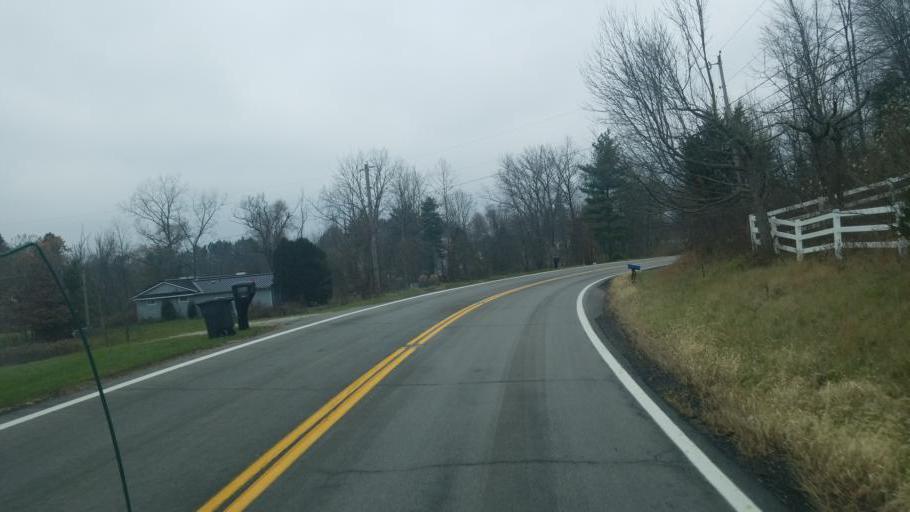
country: US
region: Ohio
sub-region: Cuyahoga County
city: North Royalton
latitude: 41.2467
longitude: -81.7267
